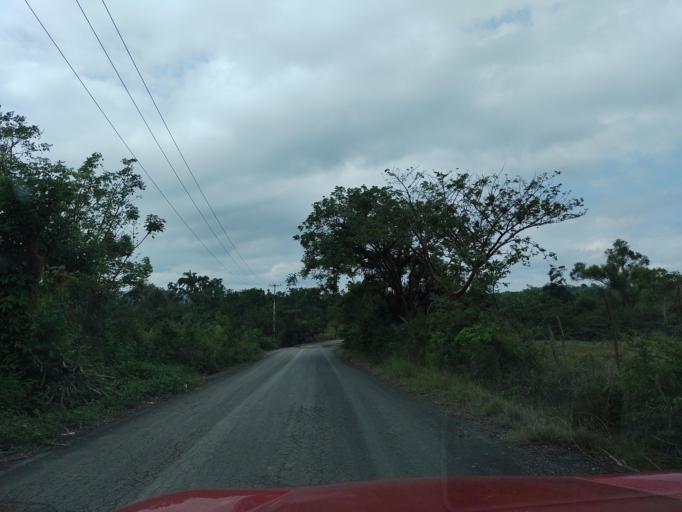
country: MX
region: Veracruz
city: Coatzintla
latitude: 20.4569
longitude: -97.4463
